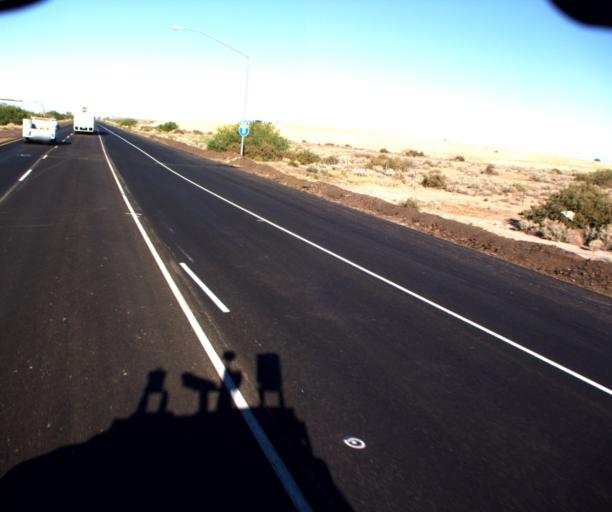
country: US
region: Arizona
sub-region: Pinal County
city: Casa Grande
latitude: 32.8282
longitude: -111.7446
